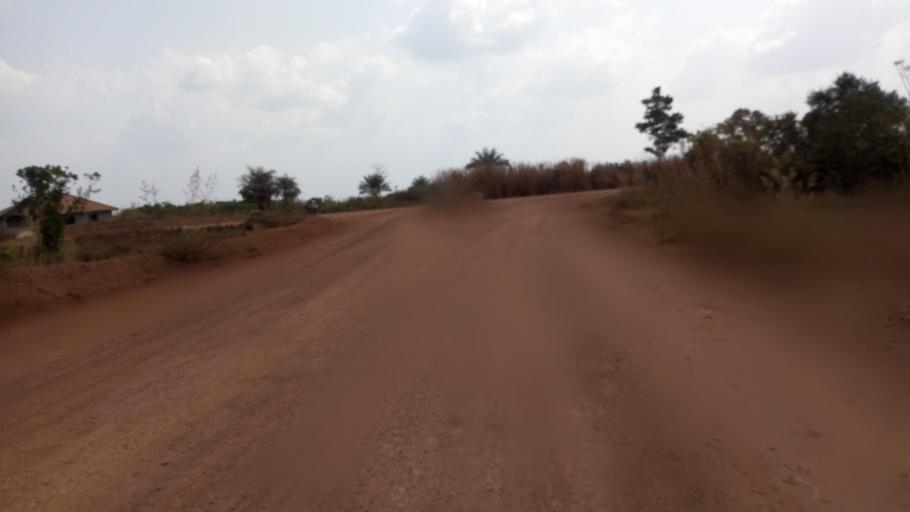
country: SL
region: Southern Province
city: Mogbwemo
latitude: 7.7846
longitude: -12.3131
